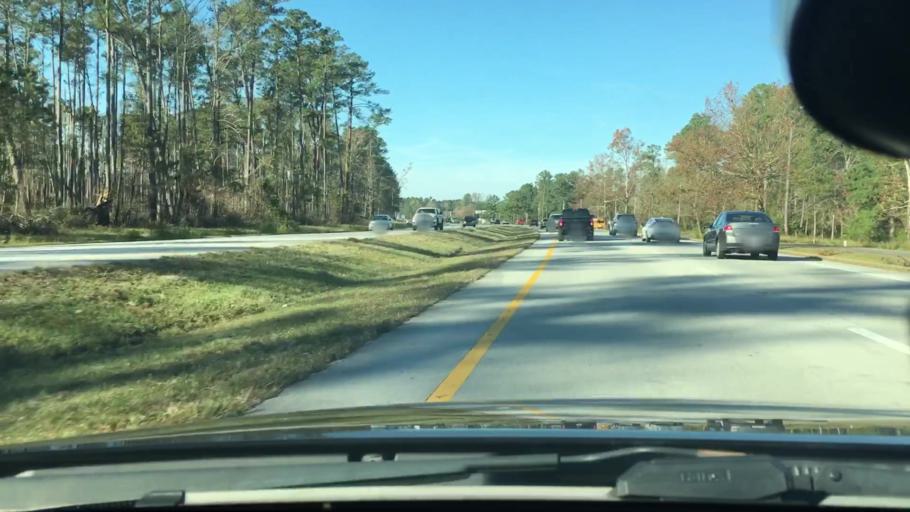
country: US
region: North Carolina
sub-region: Craven County
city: Neuse Forest
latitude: 34.9451
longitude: -76.9485
